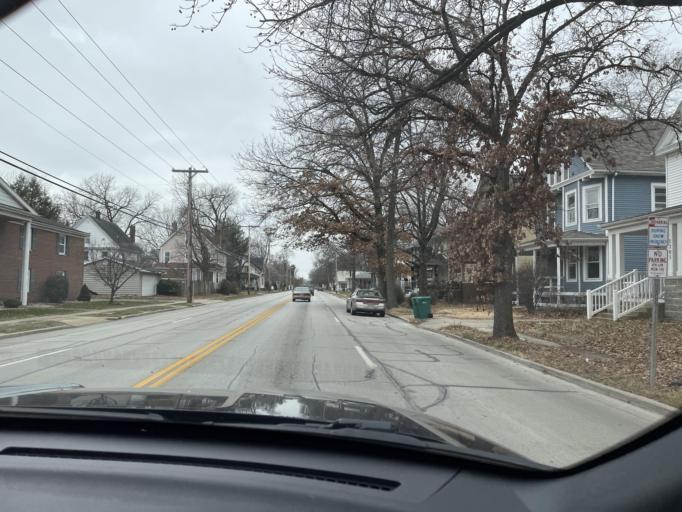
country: US
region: Illinois
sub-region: Sangamon County
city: Leland Grove
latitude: 39.7942
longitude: -89.6731
